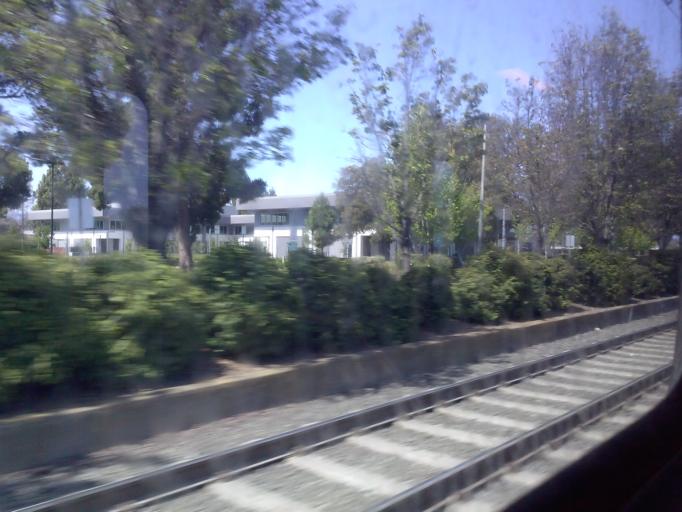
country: US
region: California
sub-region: Santa Clara County
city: Sunnyvale
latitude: 37.4112
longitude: -122.0162
